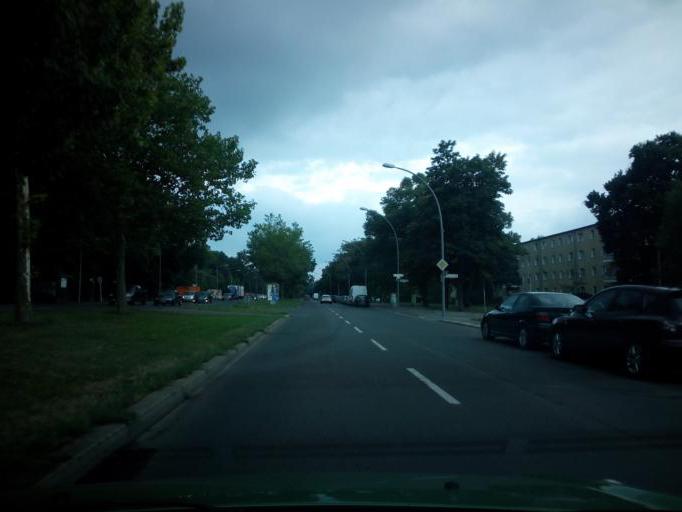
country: DE
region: Berlin
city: Oberschoneweide
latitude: 52.4621
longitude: 13.5317
